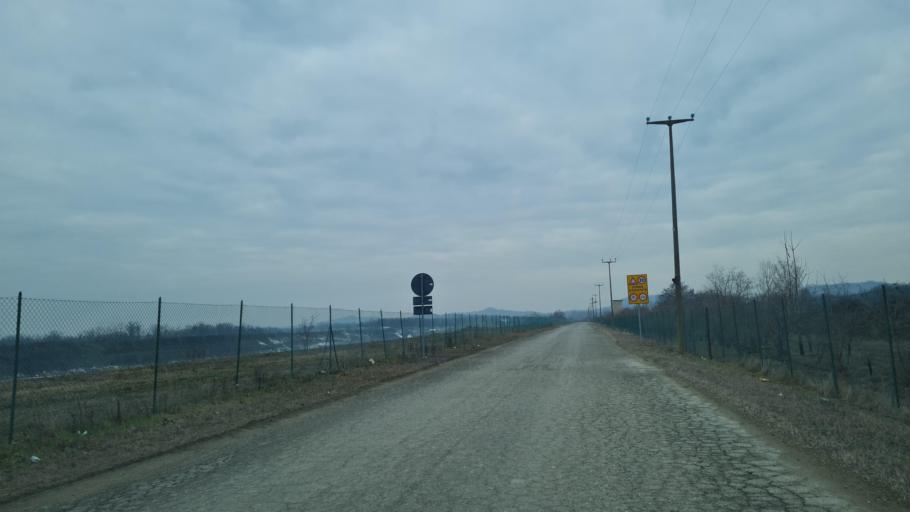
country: IT
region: Piedmont
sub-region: Provincia di Biella
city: Cavaglia
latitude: 45.3831
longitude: 8.1058
